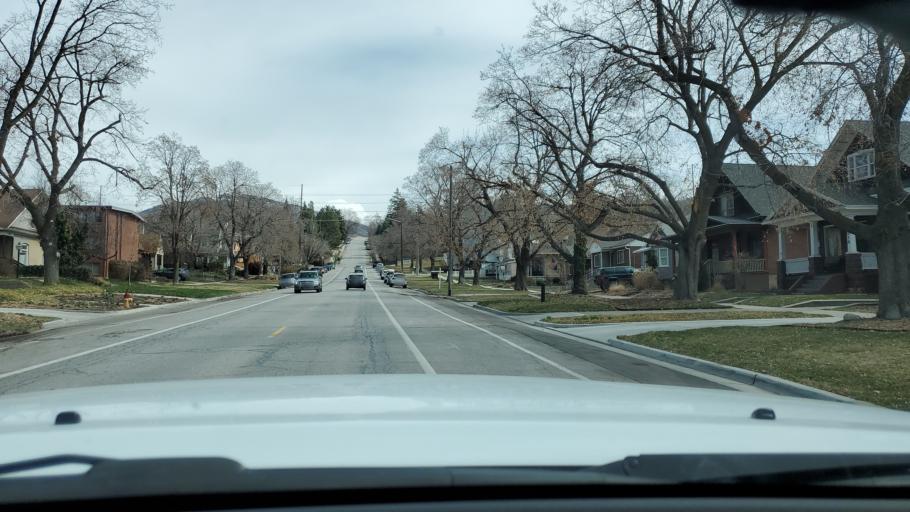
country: US
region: Utah
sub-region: Salt Lake County
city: Salt Lake City
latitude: 40.7628
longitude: -111.8621
